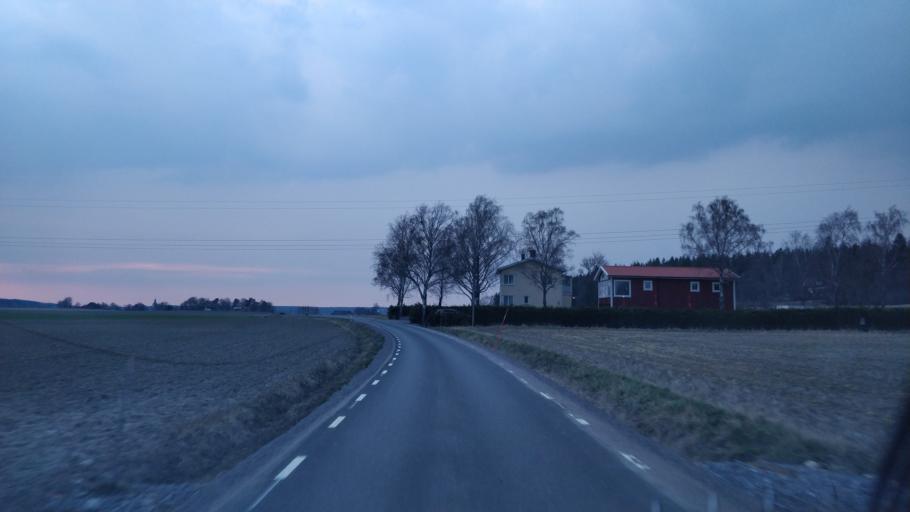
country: SE
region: Uppsala
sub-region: Enkopings Kommun
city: Orsundsbro
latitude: 59.7239
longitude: 17.2233
